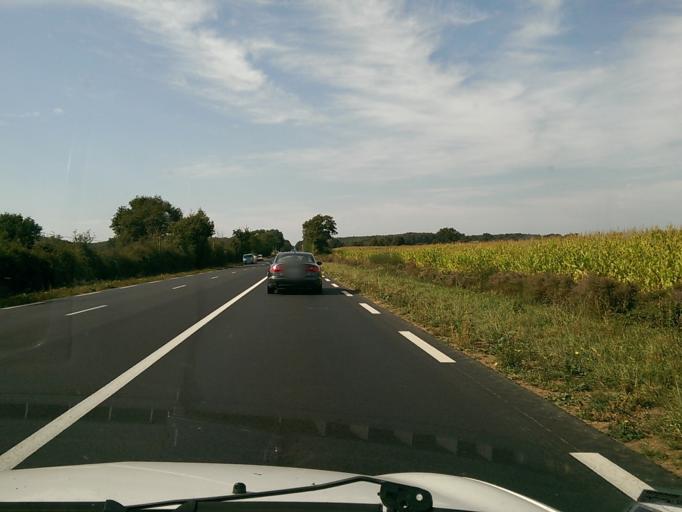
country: FR
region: Pays de la Loire
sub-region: Departement de Maine-et-Loire
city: Nueil-sur-Layon
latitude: 47.1634
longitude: -0.3906
